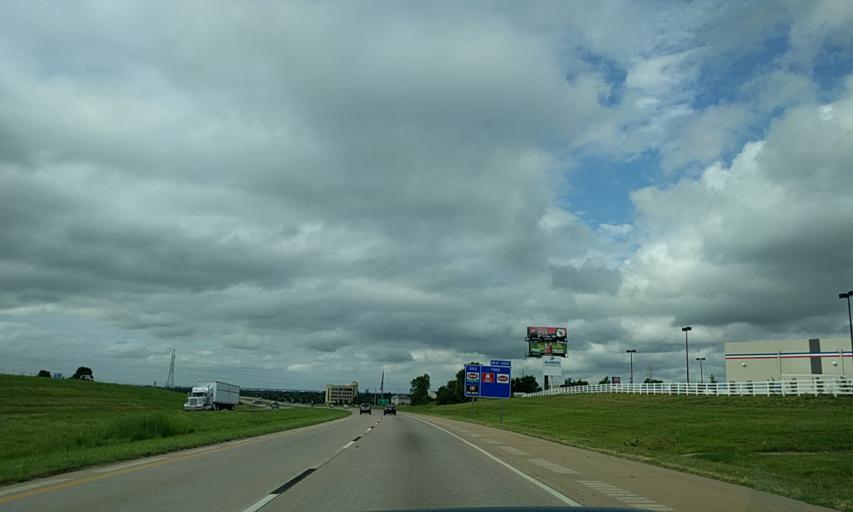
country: US
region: Oklahoma
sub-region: Tulsa County
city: Owasso
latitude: 36.2856
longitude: -95.8446
